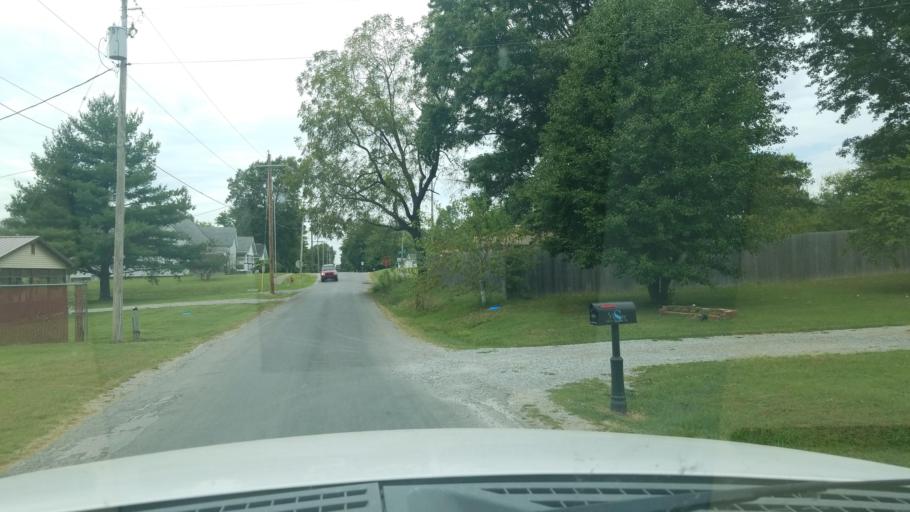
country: US
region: Illinois
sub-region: Saline County
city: Harrisburg
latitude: 37.8432
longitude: -88.6091
